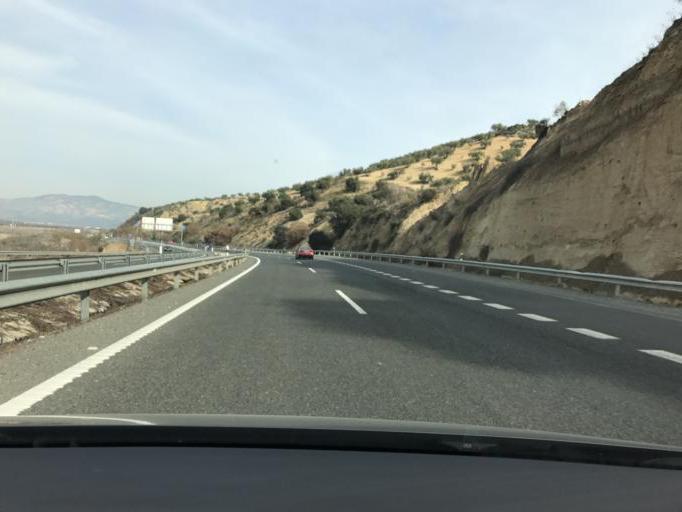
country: ES
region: Andalusia
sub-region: Provincia de Granada
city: Salar
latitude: 37.1714
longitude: -4.0835
